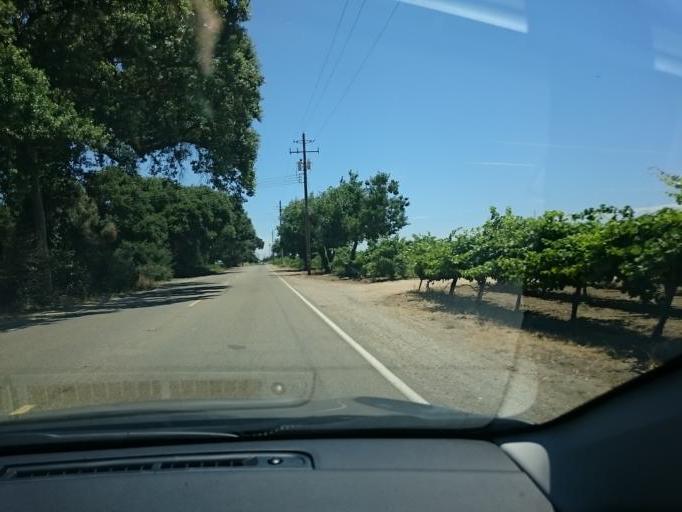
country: US
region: California
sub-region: San Joaquin County
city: Thornton
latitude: 38.1893
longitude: -121.3663
